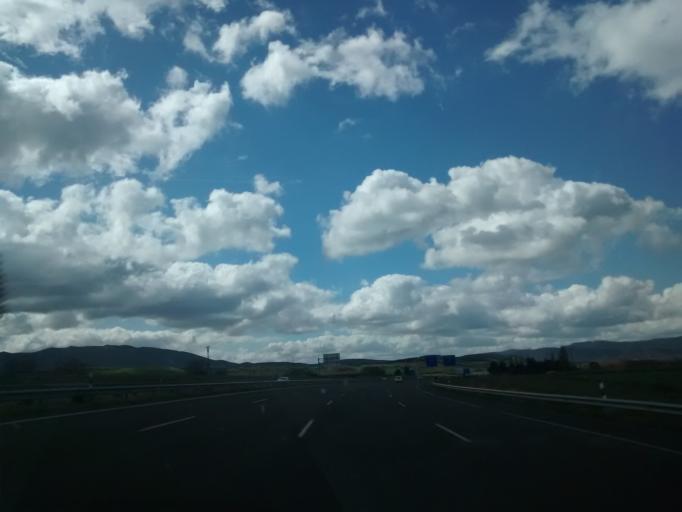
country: ES
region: Basque Country
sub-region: Provincia de Alava
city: Arminon
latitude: 42.7240
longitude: -2.8687
